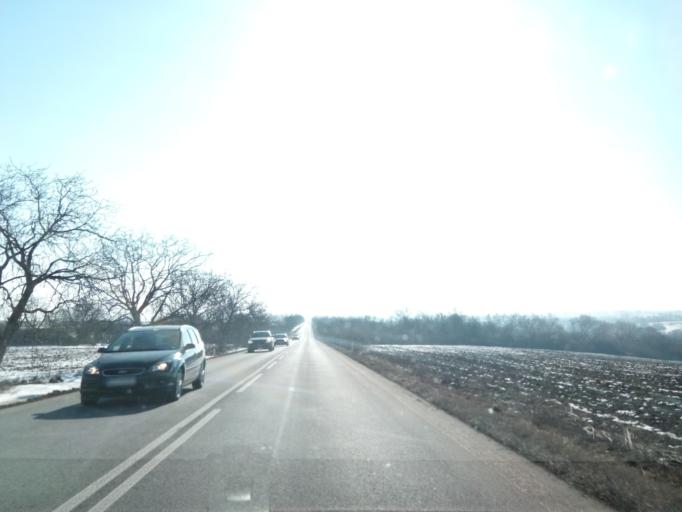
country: SK
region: Kosicky
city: Secovce
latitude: 48.7169
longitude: 21.6132
